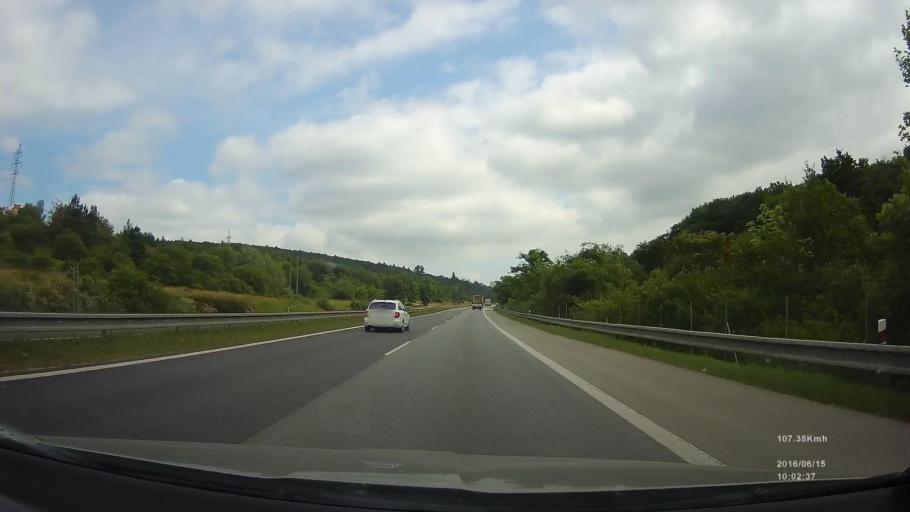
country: SK
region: Kosicky
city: Kosice
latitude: 48.7530
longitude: 21.2781
